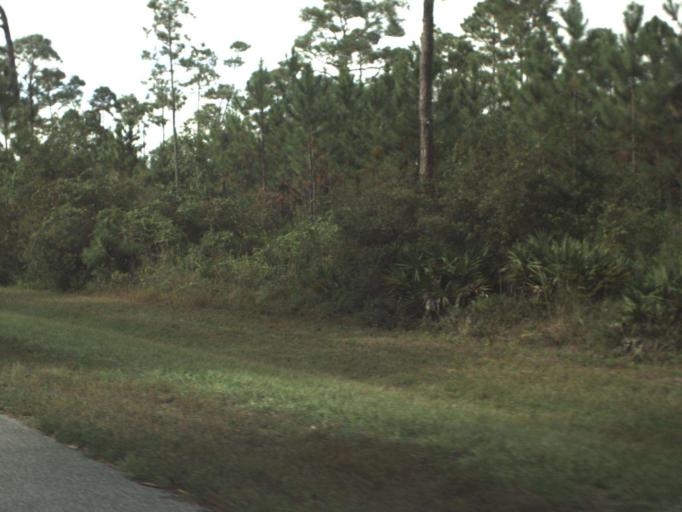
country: US
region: Florida
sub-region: Bay County
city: Mexico Beach
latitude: 29.9745
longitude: -85.4636
